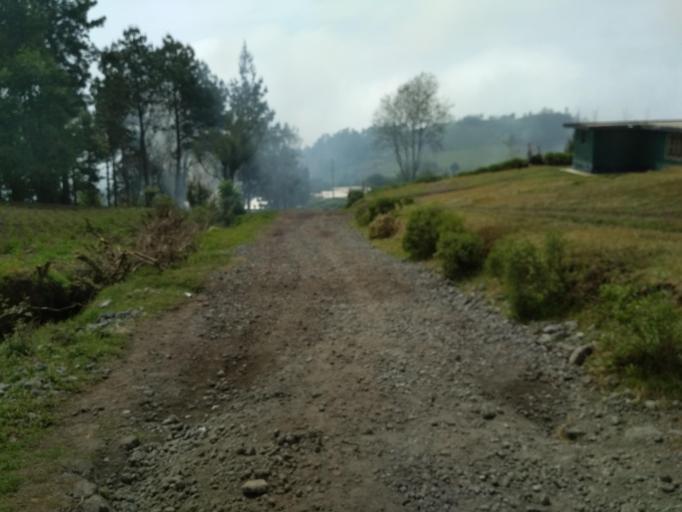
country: MX
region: Veracruz
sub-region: Mariano Escobedo
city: San Isidro el Berro
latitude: 18.9746
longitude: -97.2105
